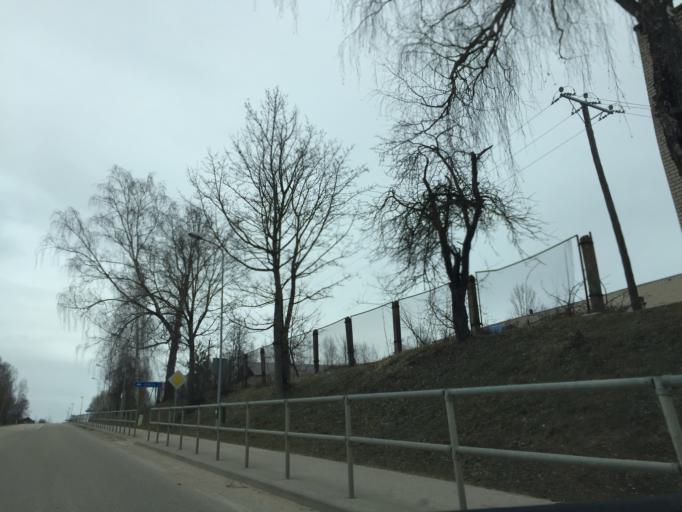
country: LV
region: Kraslavas Rajons
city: Kraslava
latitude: 55.9035
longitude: 27.1544
